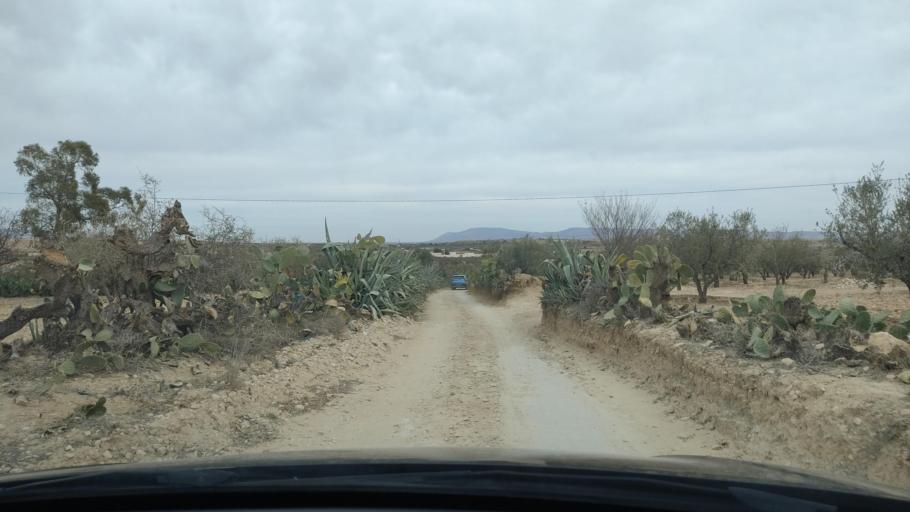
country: TN
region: Al Qasrayn
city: Kasserine
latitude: 35.2618
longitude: 8.9275
